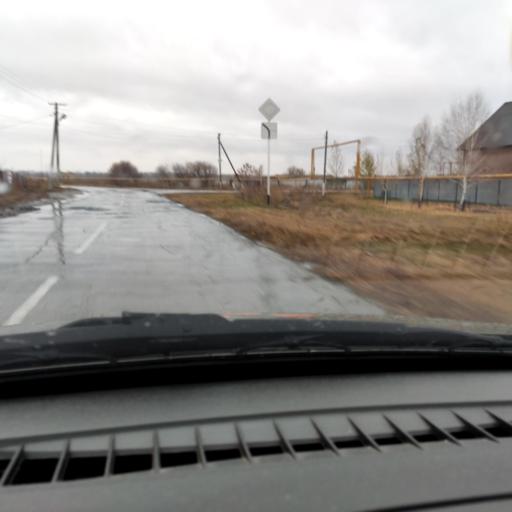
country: RU
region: Samara
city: Khryashchevka
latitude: 53.7313
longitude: 49.1784
